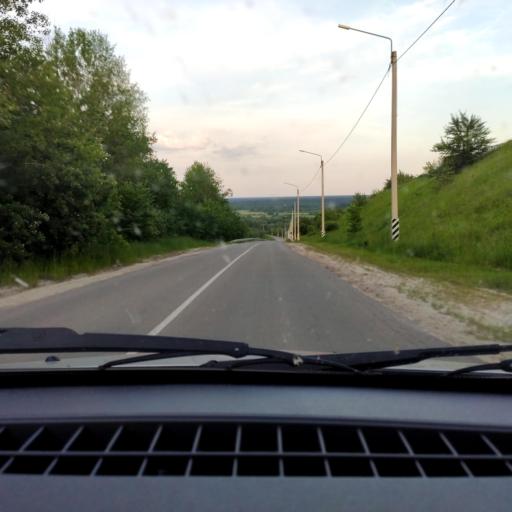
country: RU
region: Voronezj
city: Ramon'
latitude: 51.9512
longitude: 39.3679
